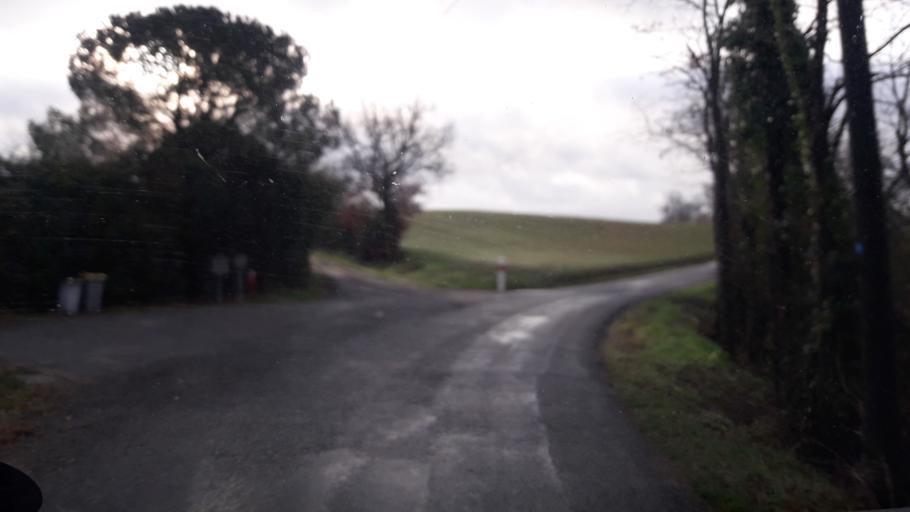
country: FR
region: Midi-Pyrenees
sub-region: Departement de la Haute-Garonne
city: Carbonne
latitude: 43.2768
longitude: 1.2510
